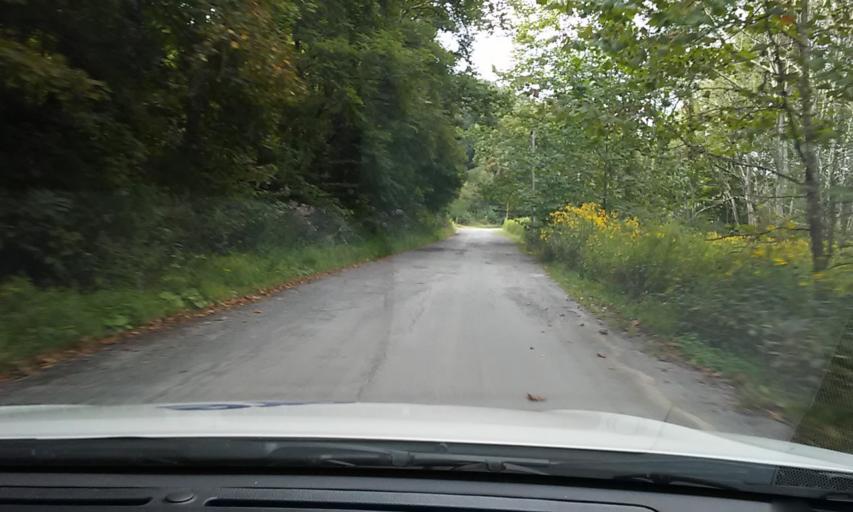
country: US
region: West Virginia
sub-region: Marion County
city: Mannington
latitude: 39.6482
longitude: -80.3522
